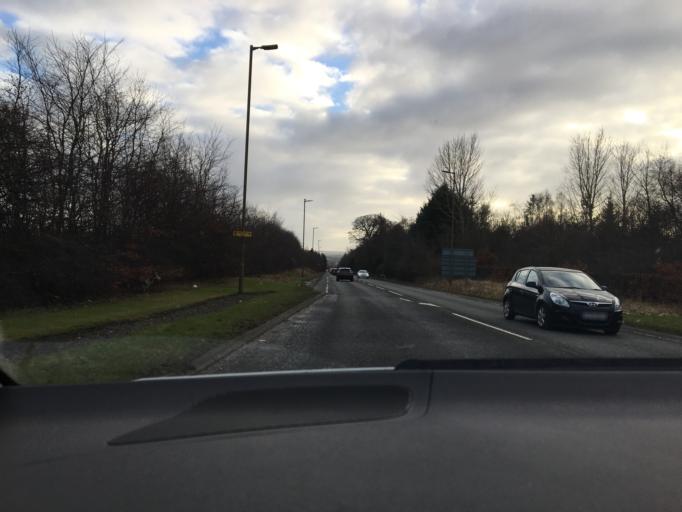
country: GB
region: Scotland
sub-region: Midlothian
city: Bonnyrigg
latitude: 55.8880
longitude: -3.0934
